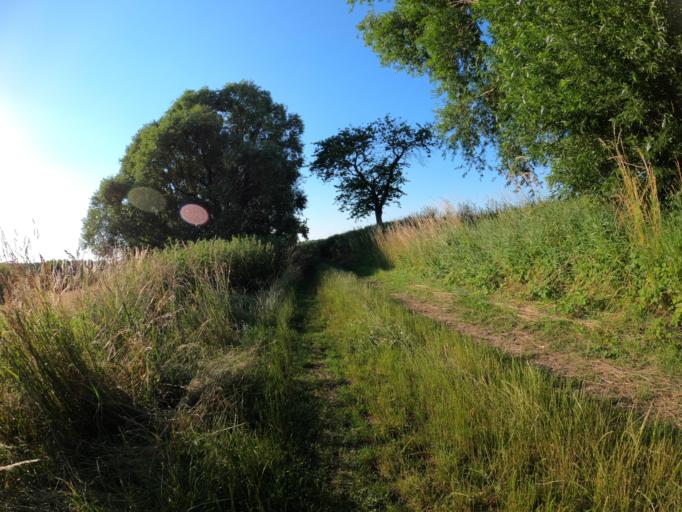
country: DE
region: Brandenburg
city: Tantow
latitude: 53.2485
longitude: 14.3660
